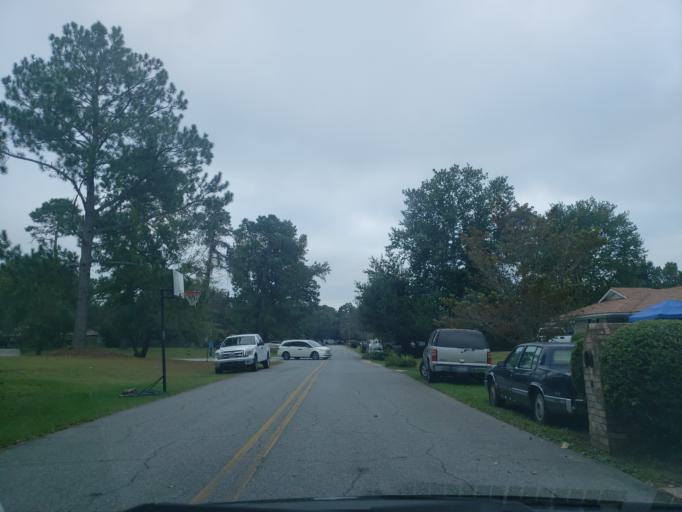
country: US
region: Georgia
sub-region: Chatham County
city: Montgomery
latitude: 31.9518
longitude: -81.1113
